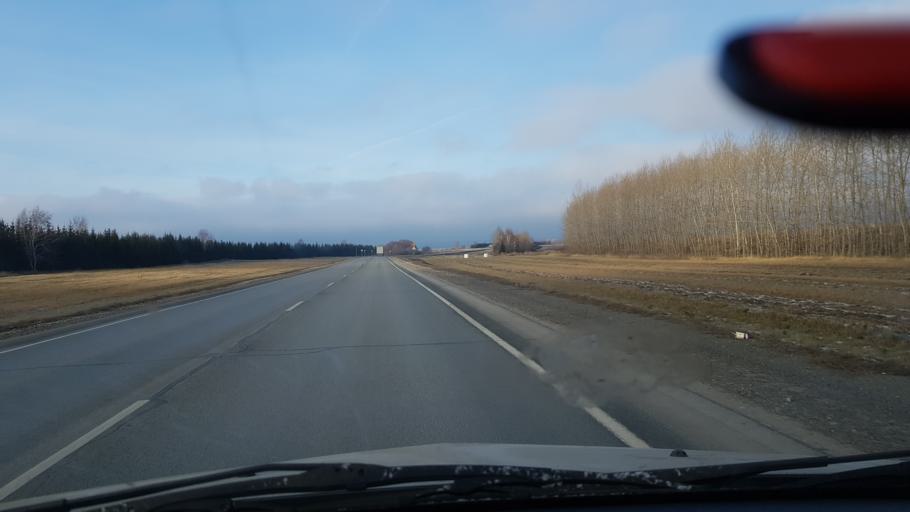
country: RU
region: Tatarstan
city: Laishevo
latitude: 55.3968
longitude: 49.7738
